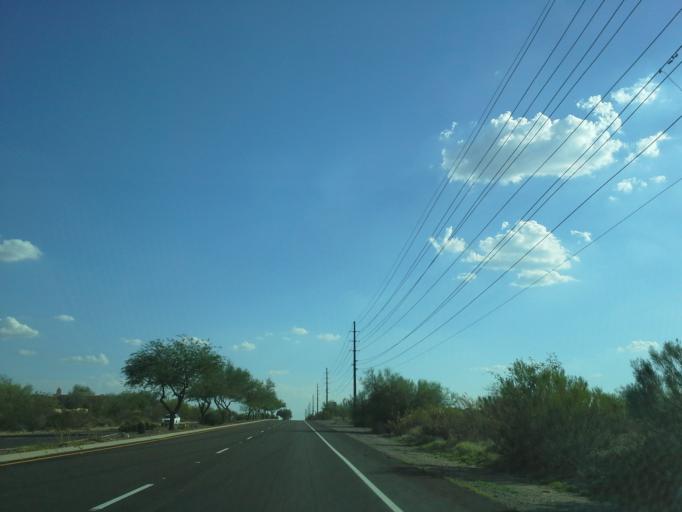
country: US
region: Arizona
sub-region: Maricopa County
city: Cave Creek
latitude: 33.8068
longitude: -111.9591
